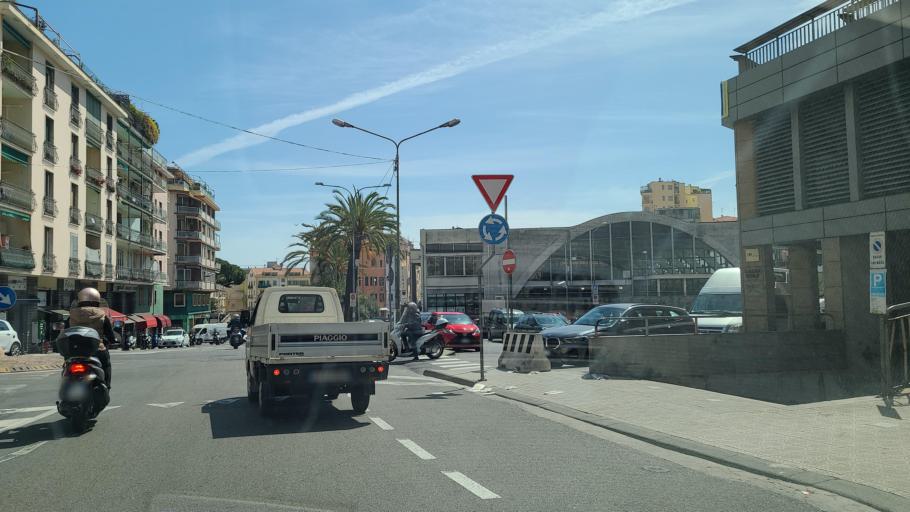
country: IT
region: Liguria
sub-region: Provincia di Imperia
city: San Remo
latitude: 43.8190
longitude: 7.7724
